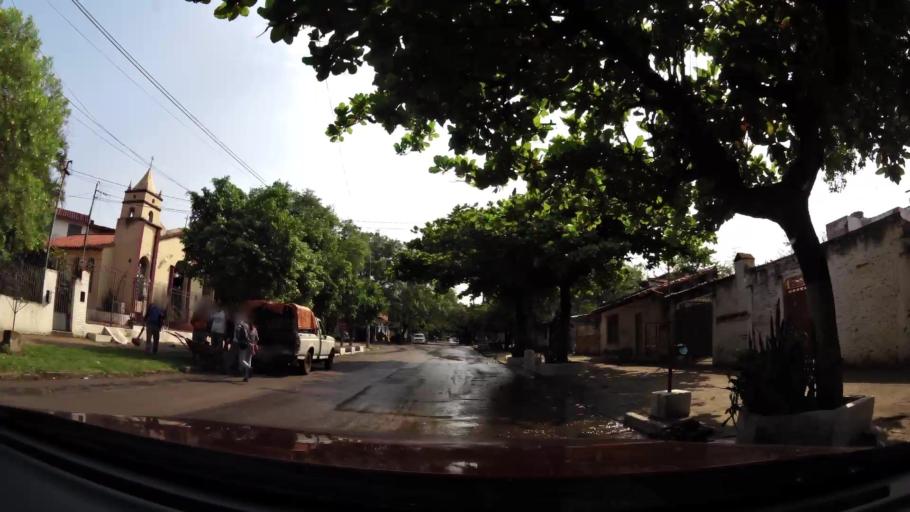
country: PY
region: Asuncion
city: Asuncion
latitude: -25.2972
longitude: -57.6617
